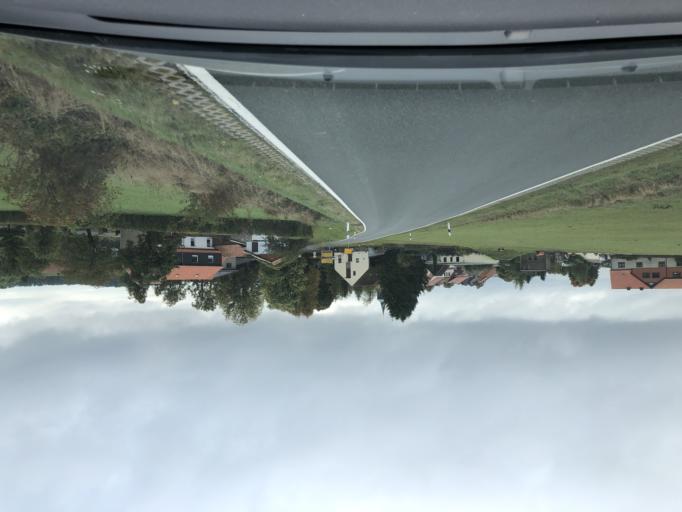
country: DE
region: Thuringia
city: Wachstedt
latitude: 51.2959
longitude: 10.2460
